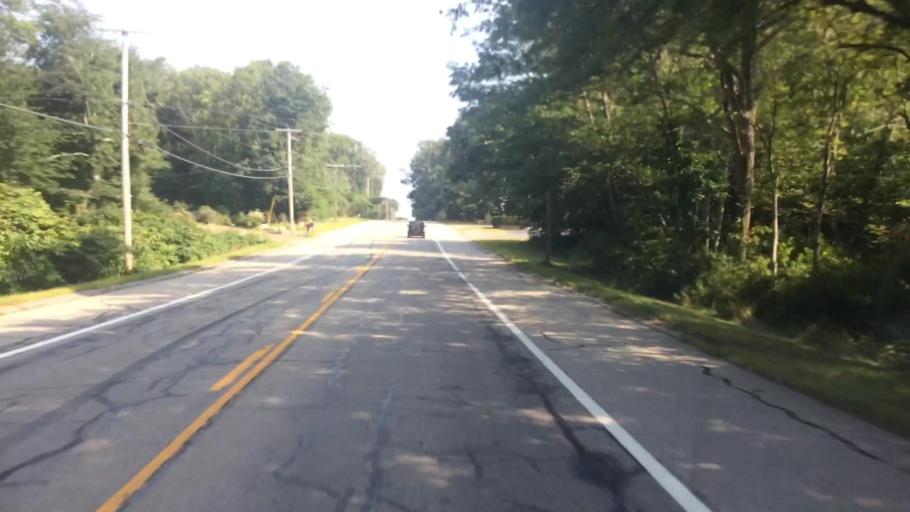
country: US
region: Rhode Island
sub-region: Washington County
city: Kingston
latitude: 41.5127
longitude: -71.5565
